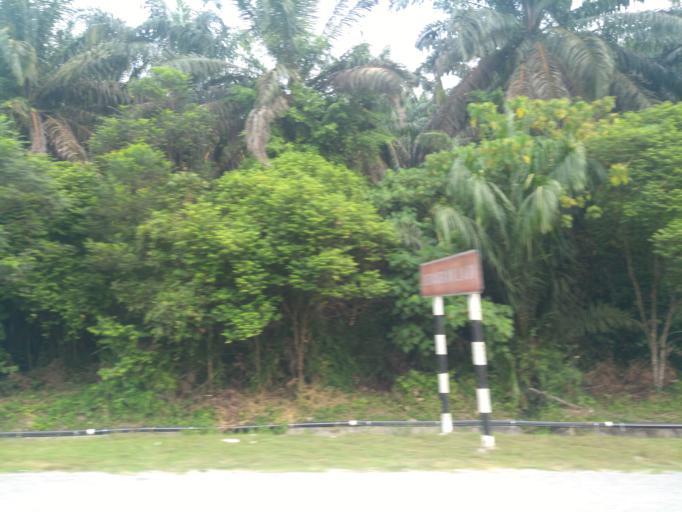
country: MY
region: Perak
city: Ipoh
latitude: 4.5546
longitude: 101.1702
